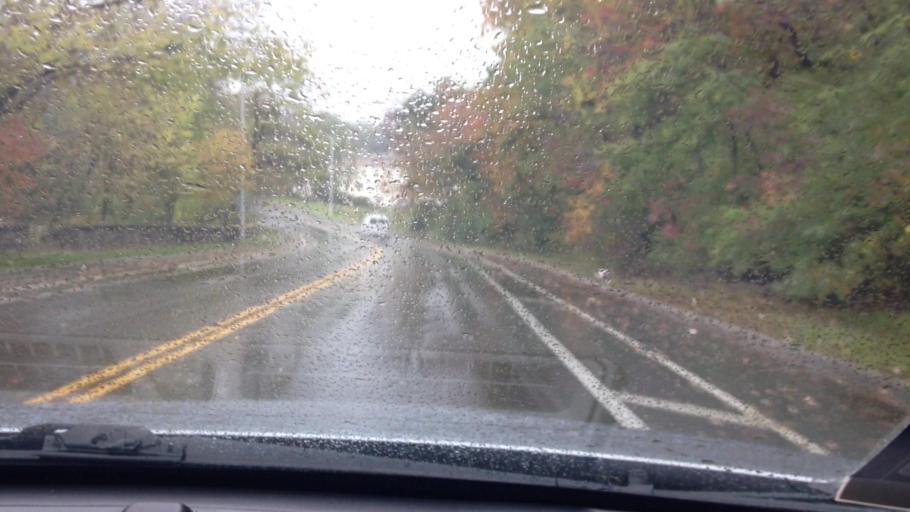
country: US
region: Missouri
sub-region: Jackson County
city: Raytown
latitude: 38.9979
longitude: -94.5395
